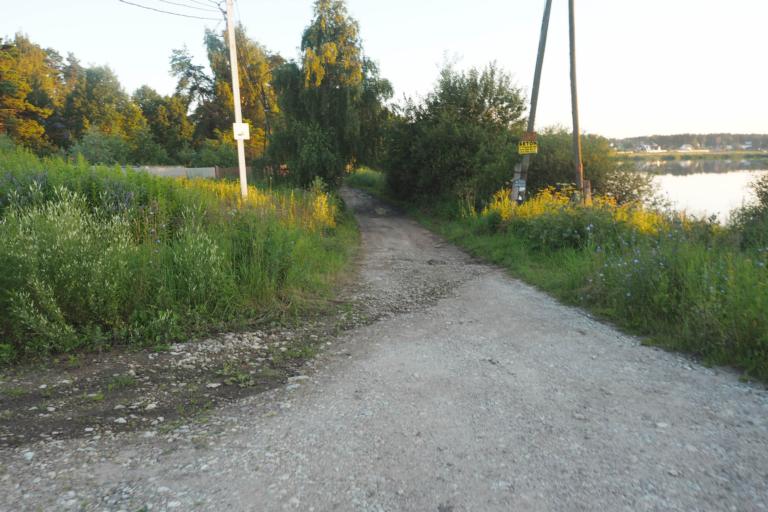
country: RU
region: Moskovskaya
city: Malyshevo
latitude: 55.5543
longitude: 38.3246
